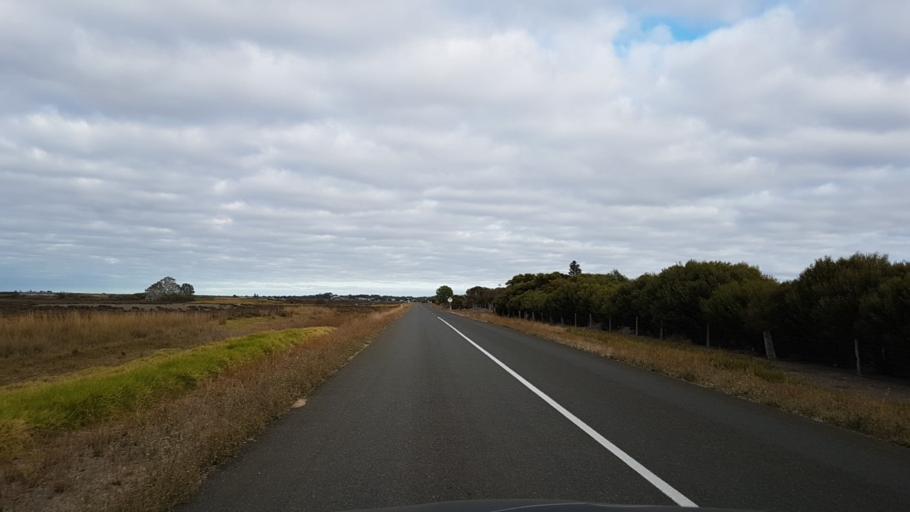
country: AU
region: South Australia
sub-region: Alexandrina
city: Langhorne Creek
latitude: -35.3949
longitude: 139.0035
